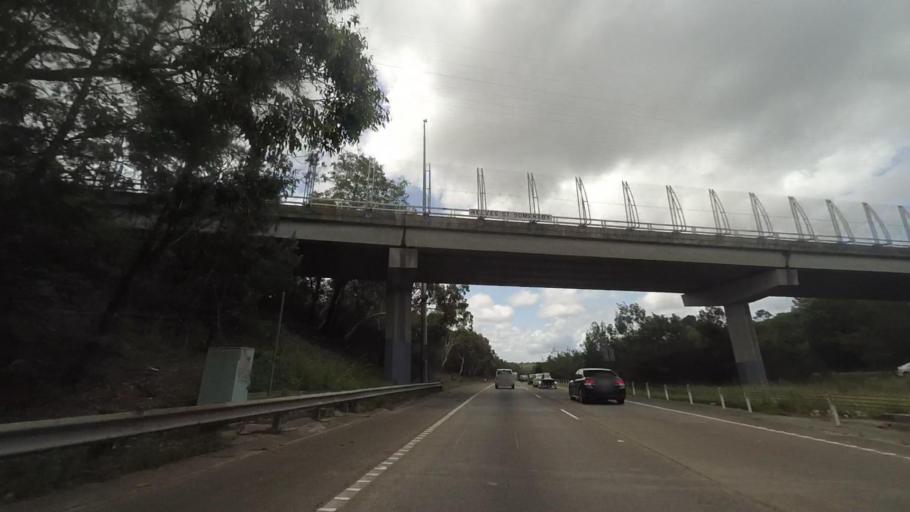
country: AU
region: New South Wales
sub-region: Gosford Shire
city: Narara
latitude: -33.3957
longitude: 151.2969
